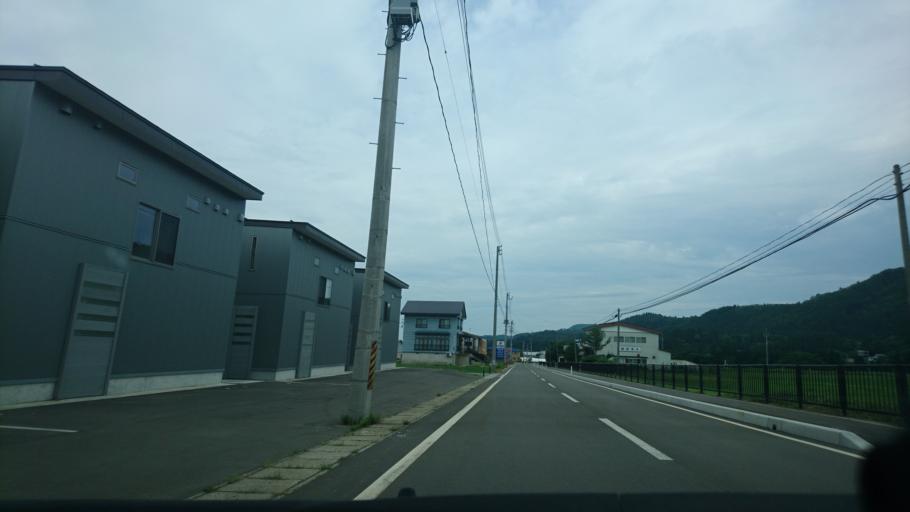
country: JP
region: Akita
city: Yuzawa
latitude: 39.1818
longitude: 140.6427
